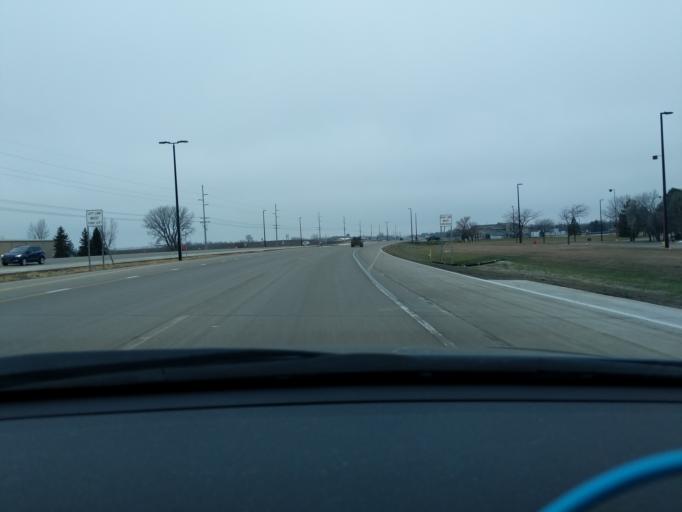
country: US
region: Minnesota
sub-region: Lyon County
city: Marshall
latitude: 44.4449
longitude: -95.7587
